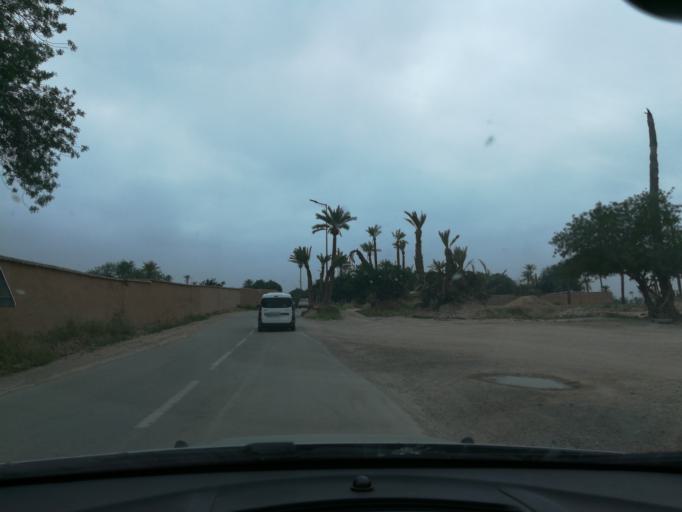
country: MA
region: Marrakech-Tensift-Al Haouz
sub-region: Marrakech
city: Marrakesh
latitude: 31.6629
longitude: -7.9686
